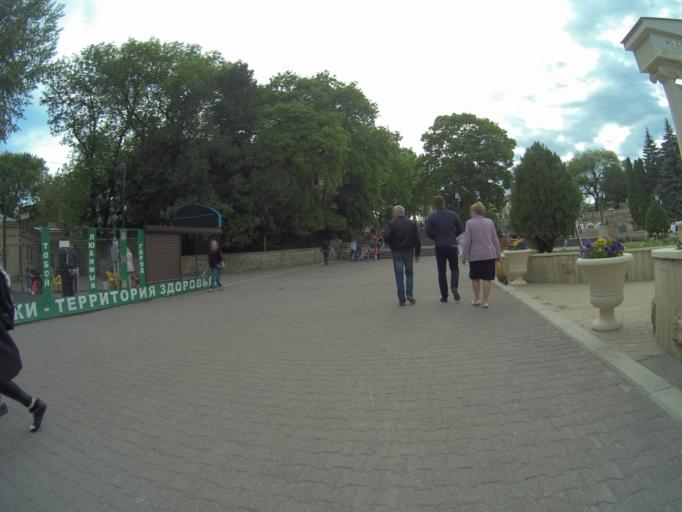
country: RU
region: Stavropol'skiy
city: Yessentuki
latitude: 44.0444
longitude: 42.8606
